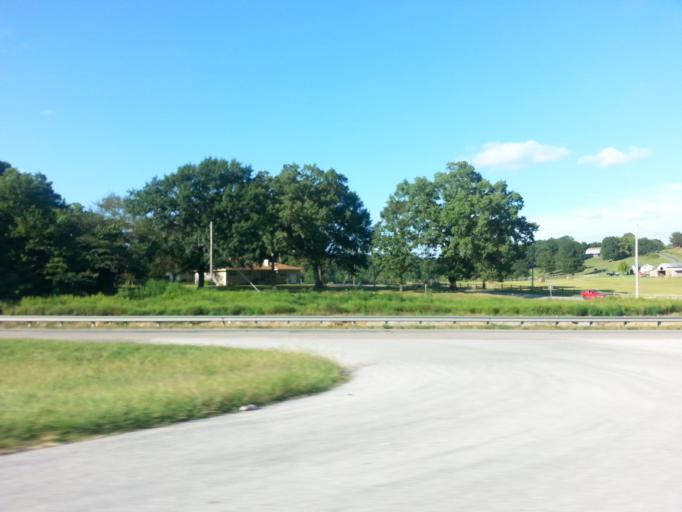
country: US
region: Alabama
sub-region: Colbert County
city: Tuscumbia
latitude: 34.7126
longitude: -87.7769
